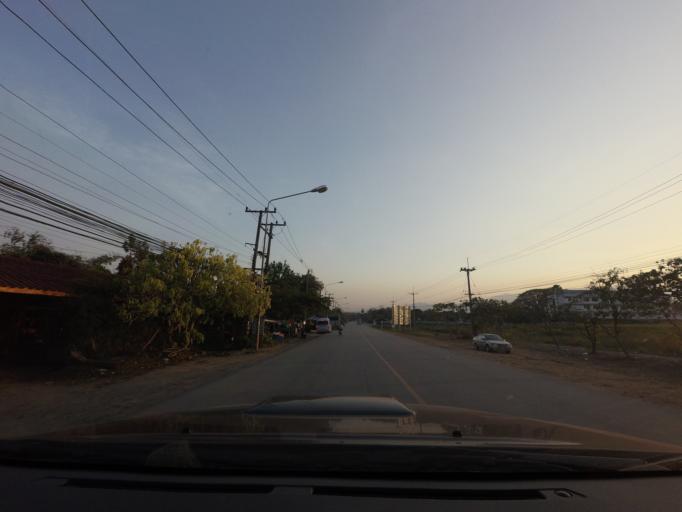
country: TH
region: Chiang Mai
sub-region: Amphoe Chiang Dao
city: Chiang Dao
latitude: 19.3597
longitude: 98.9645
